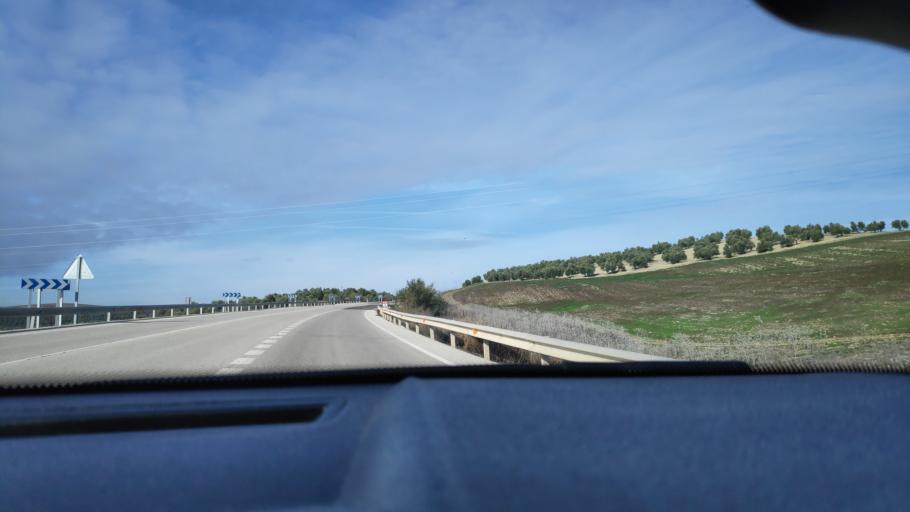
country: ES
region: Andalusia
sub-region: Provincia de Jaen
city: Linares
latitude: 38.0776
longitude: -3.6136
